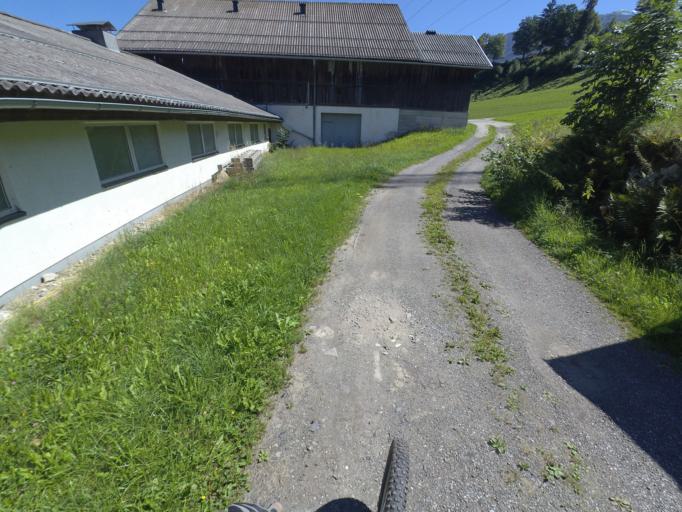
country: AT
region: Salzburg
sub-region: Politischer Bezirk Sankt Johann im Pongau
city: Sankt Veit im Pongau
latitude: 47.3247
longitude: 13.1281
